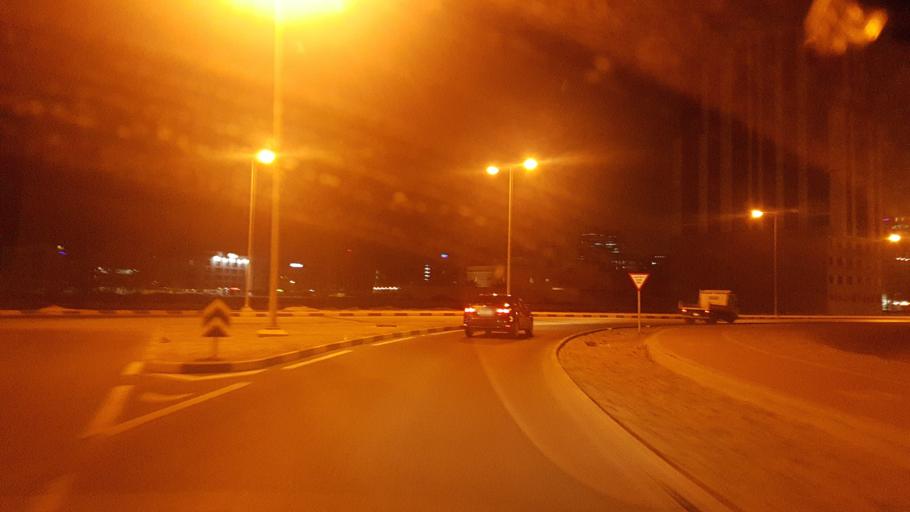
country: BH
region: Manama
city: Jidd Hafs
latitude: 26.2371
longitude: 50.5255
